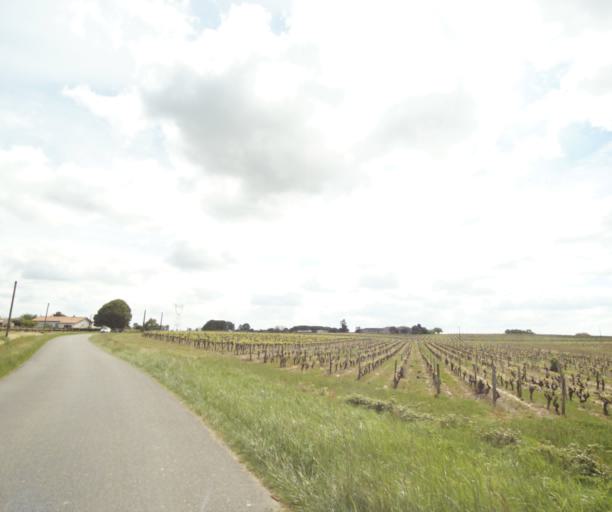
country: FR
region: Poitou-Charentes
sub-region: Departement de la Charente-Maritime
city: Cherac
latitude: 45.7421
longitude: -0.4517
